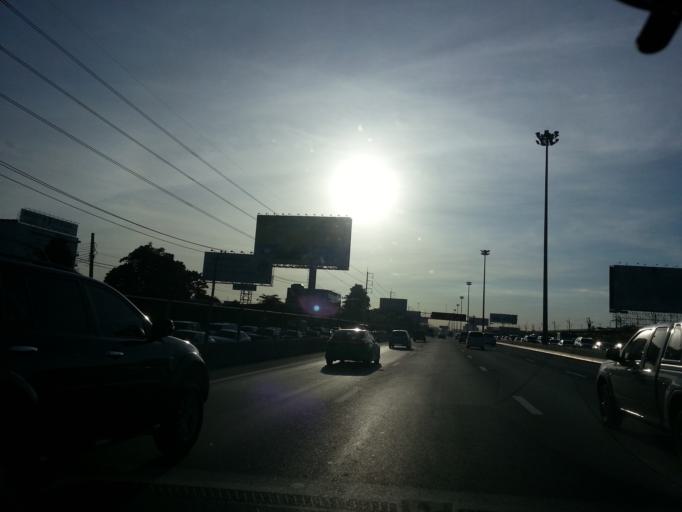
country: TH
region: Bangkok
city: Suan Luang
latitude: 13.7352
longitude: 100.6800
